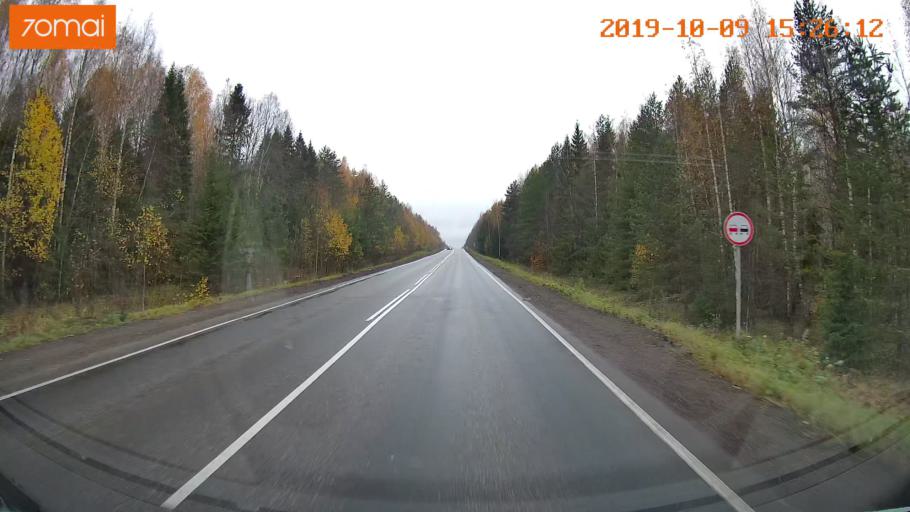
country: RU
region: Kostroma
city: Susanino
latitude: 58.0217
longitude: 41.4098
